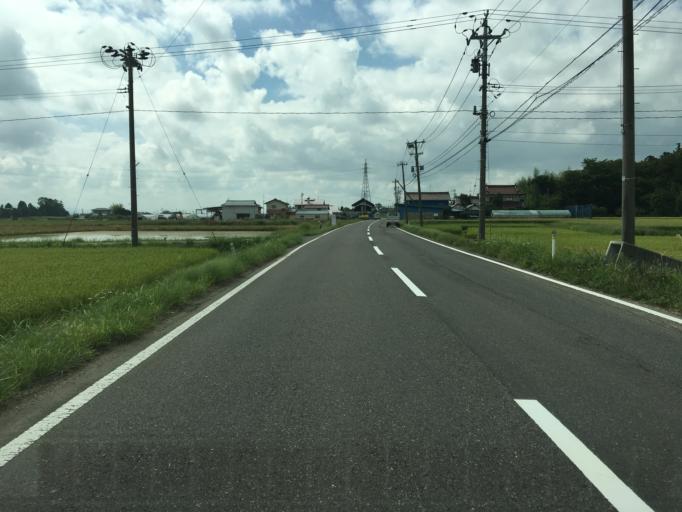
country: JP
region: Fukushima
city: Motomiya
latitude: 37.4690
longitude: 140.3406
